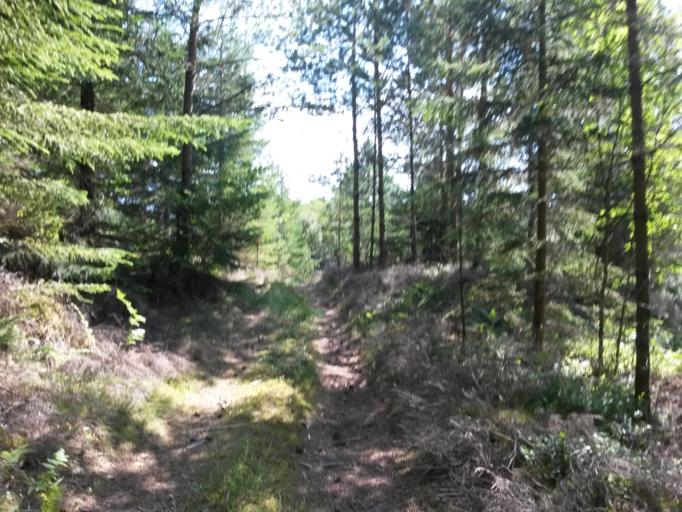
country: SE
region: Vaestra Goetaland
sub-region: Vargarda Kommun
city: Jonstorp
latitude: 57.9640
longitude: 12.6844
